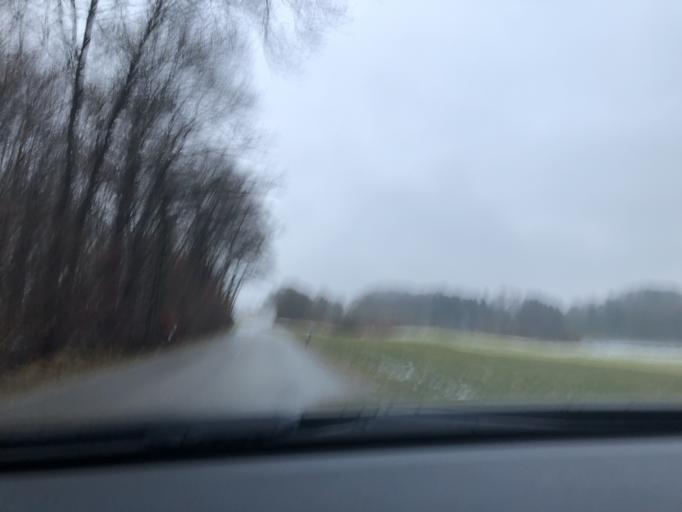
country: DE
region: Bavaria
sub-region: Upper Bavaria
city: Worthsee
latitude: 48.0826
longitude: 11.1854
